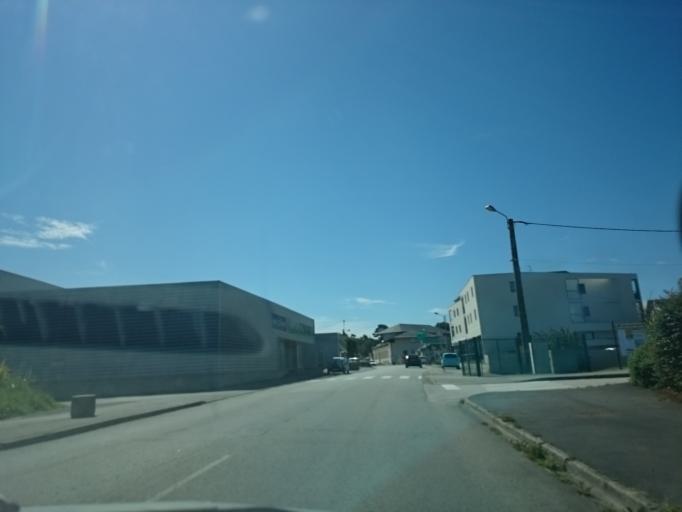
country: FR
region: Brittany
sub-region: Departement du Finistere
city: Saint-Renan
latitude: 48.4357
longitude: -4.6221
